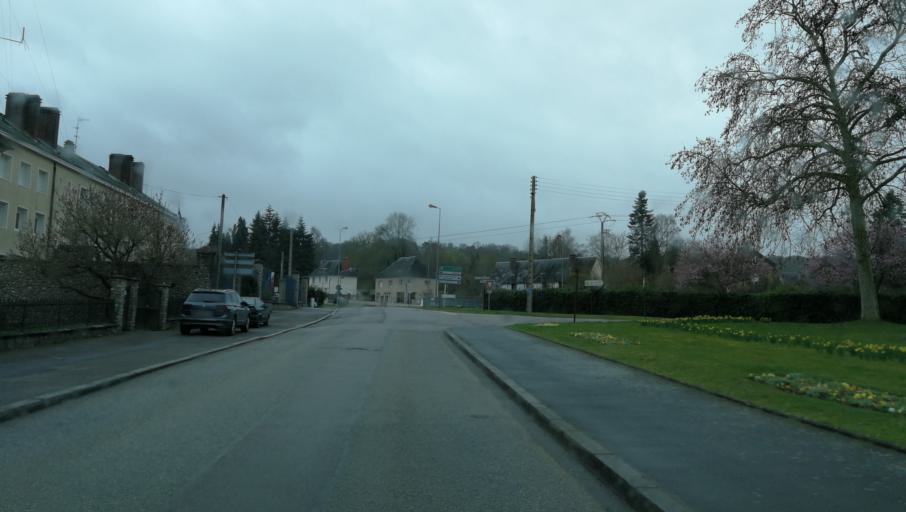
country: FR
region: Haute-Normandie
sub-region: Departement de l'Eure
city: Brionne
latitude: 49.1927
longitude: 0.7125
